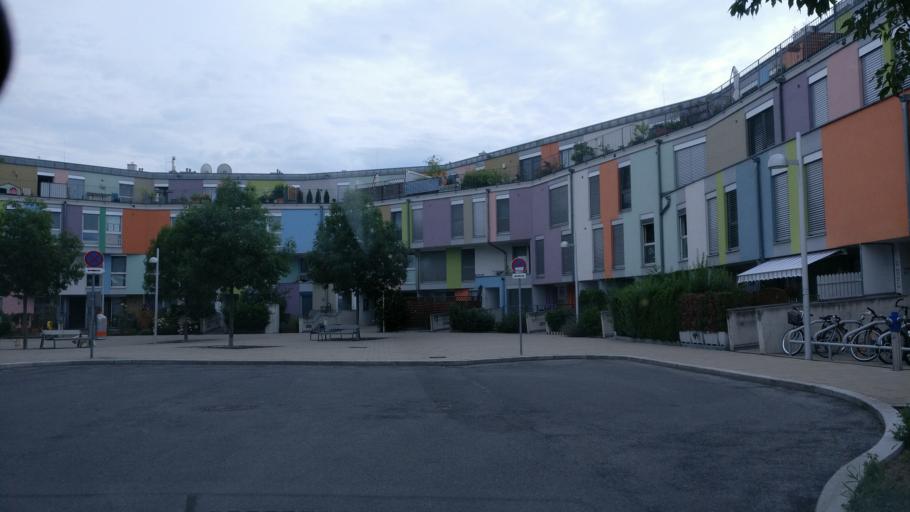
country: AT
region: Lower Austria
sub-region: Politischer Bezirk Korneuburg
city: Hagenbrunn
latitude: 48.2930
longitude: 16.4109
